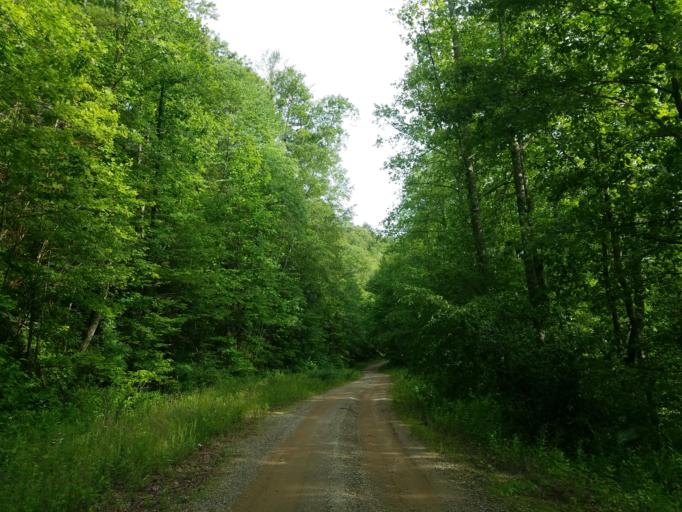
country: US
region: Georgia
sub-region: Union County
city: Blairsville
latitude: 34.7557
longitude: -84.0122
